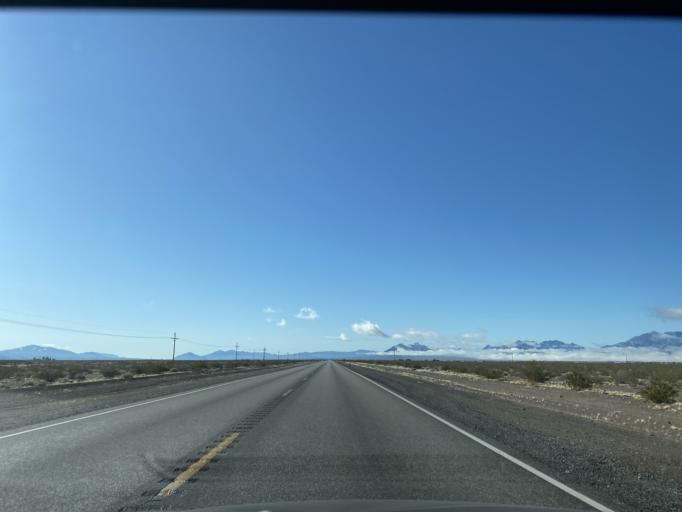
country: US
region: Nevada
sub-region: Nye County
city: Beatty
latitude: 36.5881
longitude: -116.4103
